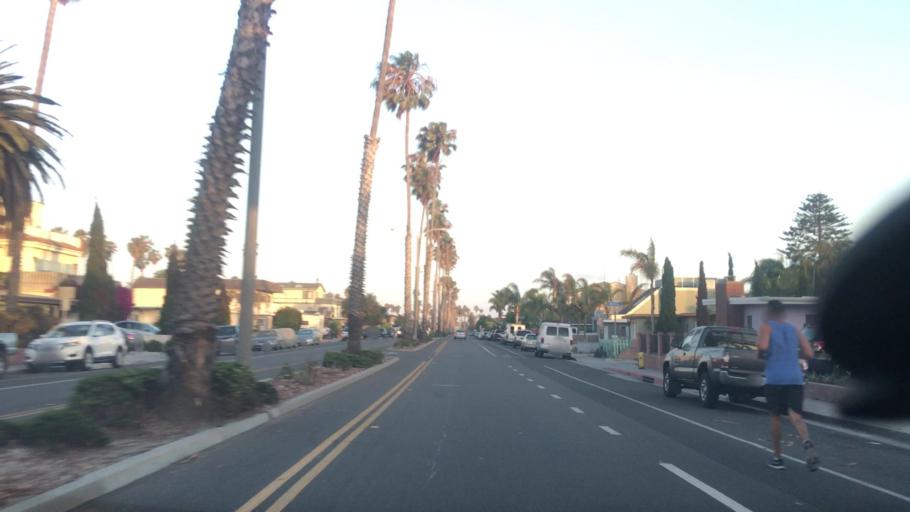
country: US
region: California
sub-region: Ventura County
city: Ventura
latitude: 34.2630
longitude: -119.2712
